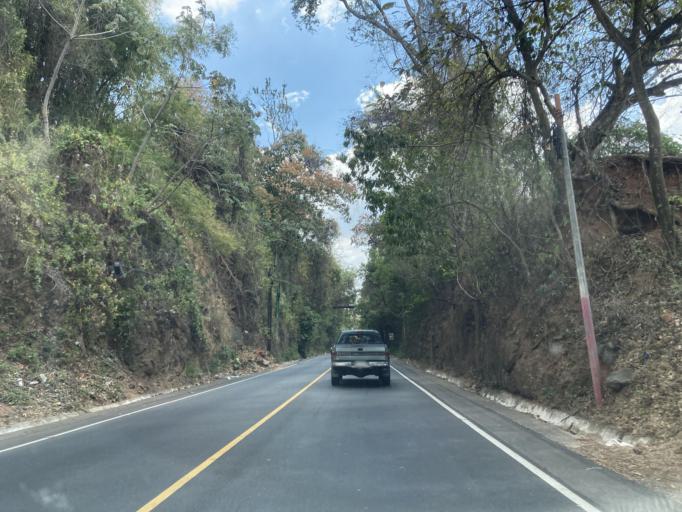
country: GT
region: Santa Rosa
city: Guazacapan
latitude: 14.0714
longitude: -90.4235
